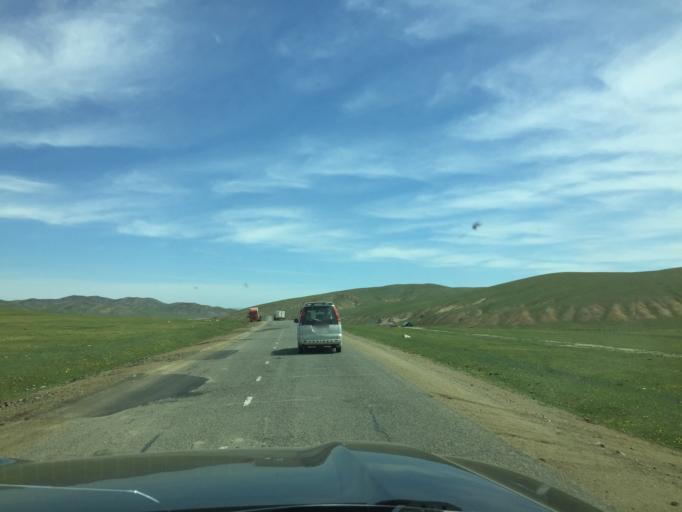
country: MN
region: Central Aimak
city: Bornuur
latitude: 48.6676
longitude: 106.1331
